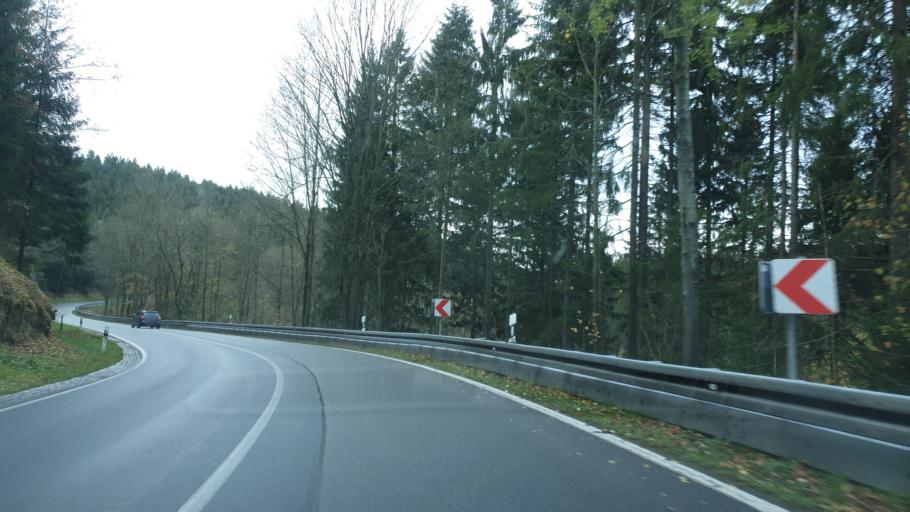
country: DE
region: Saxony
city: Eibenstock
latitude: 50.5028
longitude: 12.5676
